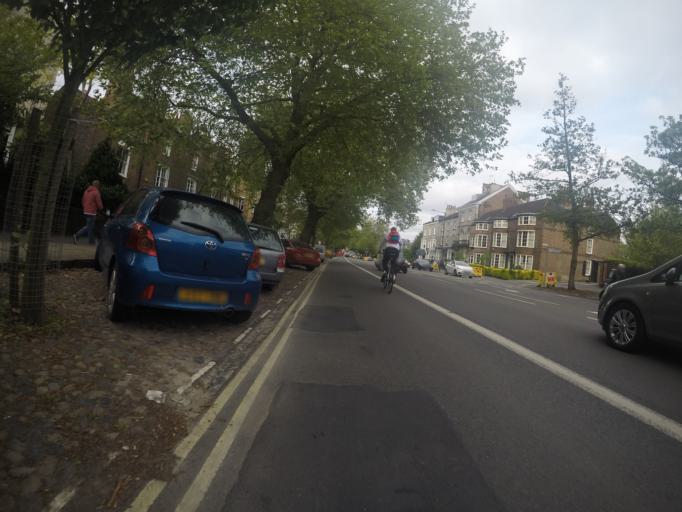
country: GB
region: England
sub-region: City of York
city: York
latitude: 53.9522
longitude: -1.0964
